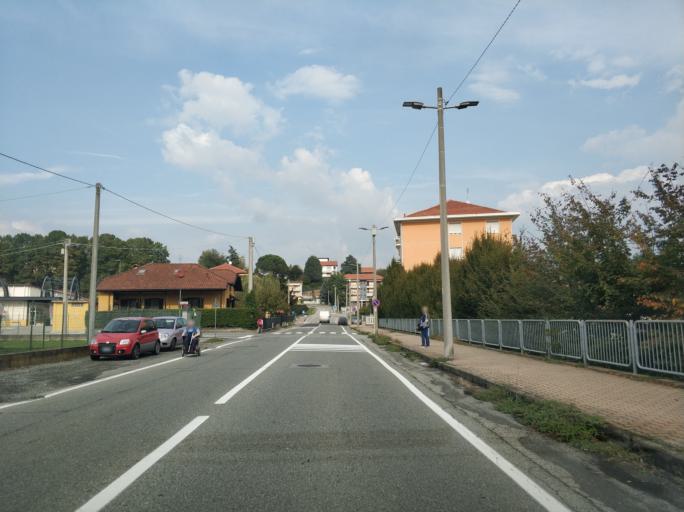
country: IT
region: Piedmont
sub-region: Provincia di Torino
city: San Carlo Canavese
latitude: 45.2408
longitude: 7.6073
